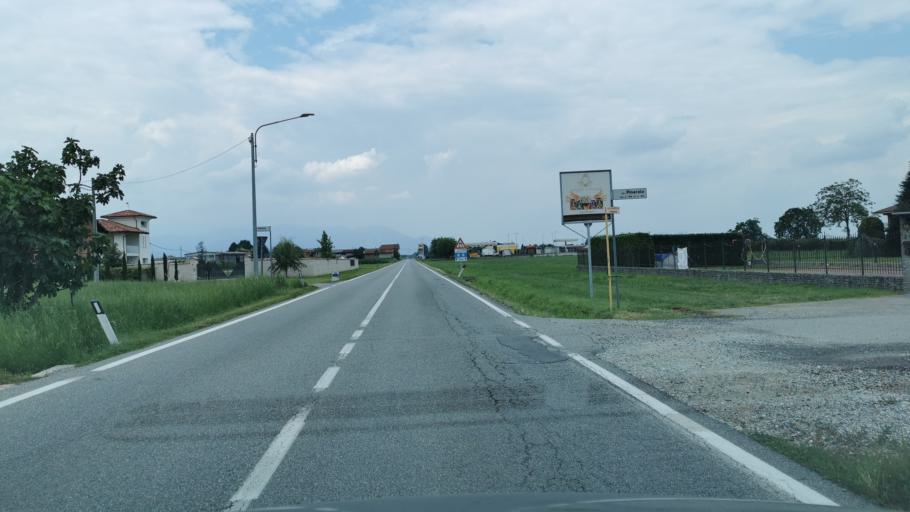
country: IT
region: Piedmont
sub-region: Provincia di Torino
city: Cavour
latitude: 44.8037
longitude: 7.3732
